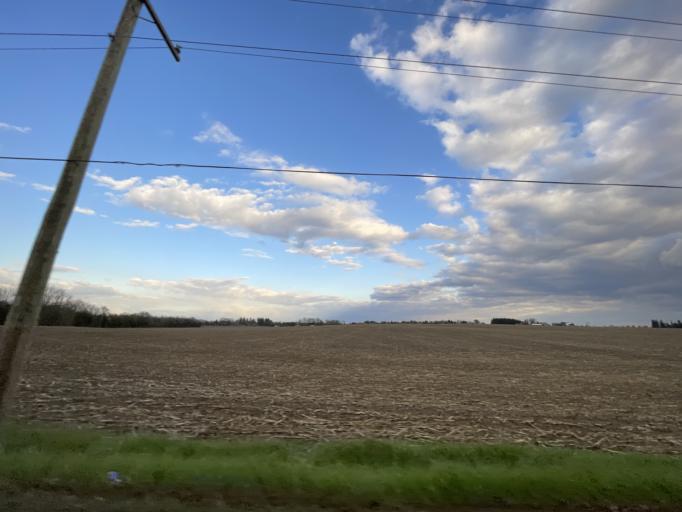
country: CA
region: Ontario
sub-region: Wellington County
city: Guelph
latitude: 43.5907
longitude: -80.2926
